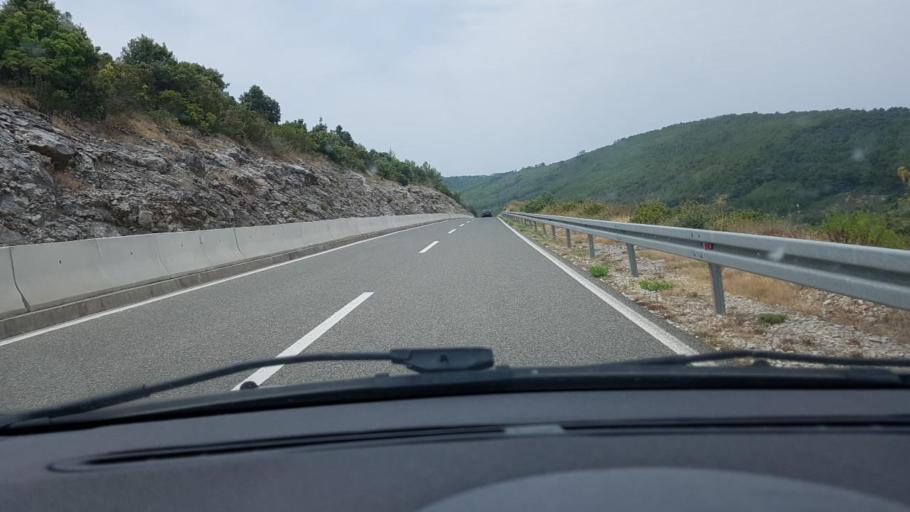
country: HR
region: Dubrovacko-Neretvanska
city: Smokvica
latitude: 42.9543
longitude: 16.9127
